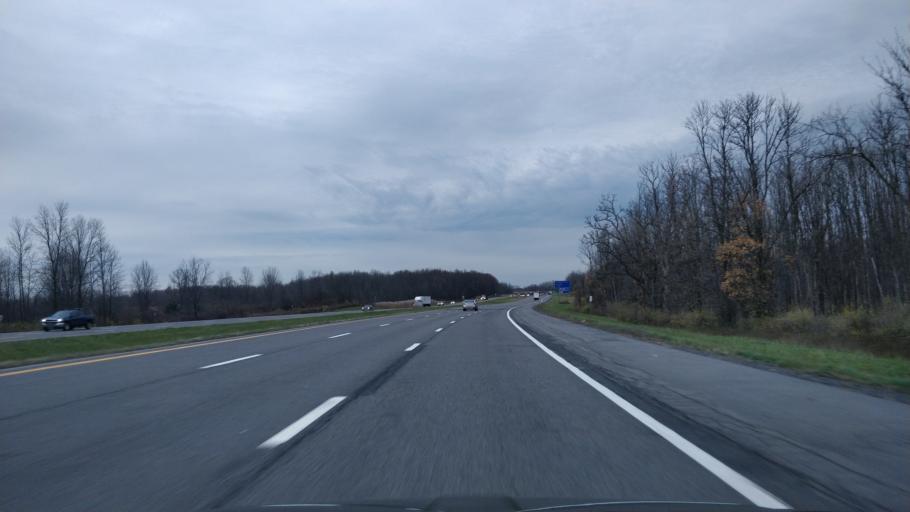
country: US
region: New York
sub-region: Onondaga County
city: Brewerton
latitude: 43.2190
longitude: -76.1296
